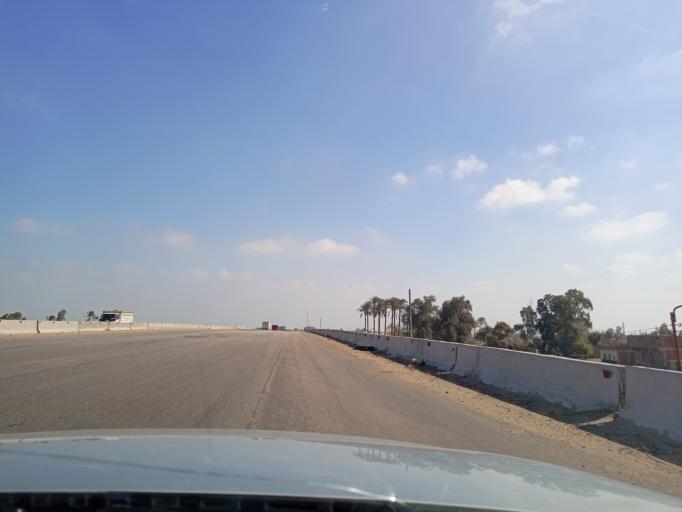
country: EG
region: Eastern Province
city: Mashtul as Suq
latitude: 30.4621
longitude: 31.3655
